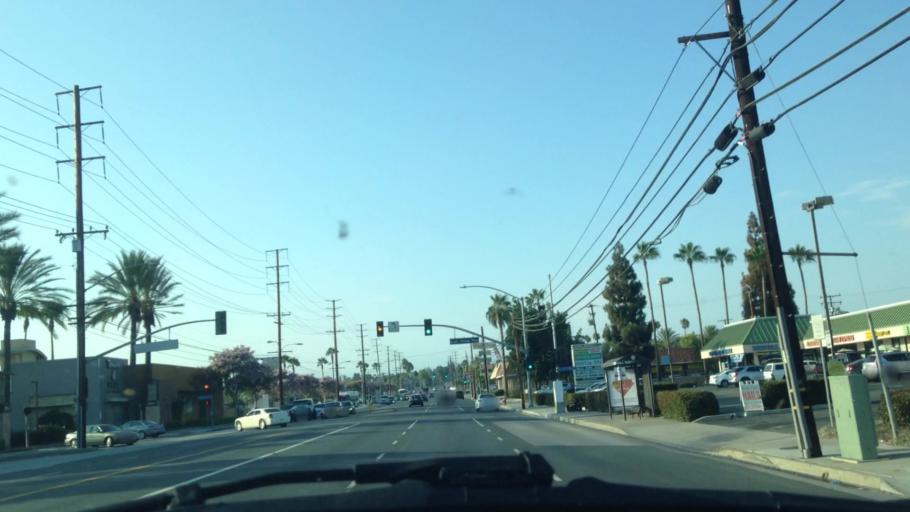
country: US
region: California
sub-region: Orange County
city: Villa Park
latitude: 33.8255
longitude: -117.8360
